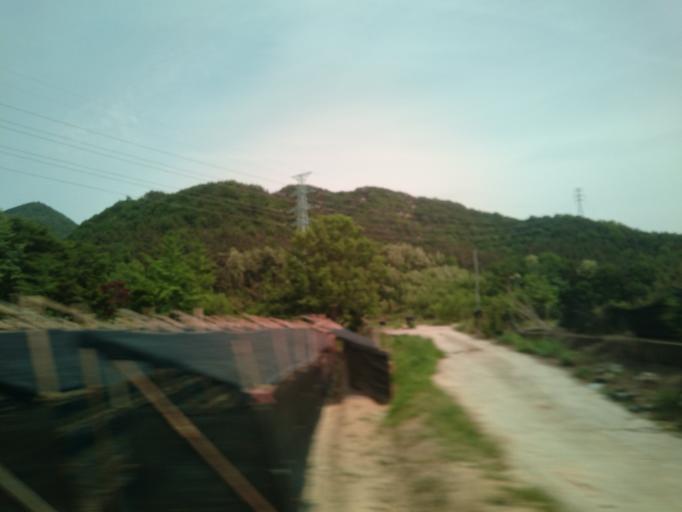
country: KR
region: Jeollabuk-do
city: Wanju
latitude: 35.8993
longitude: 127.1942
